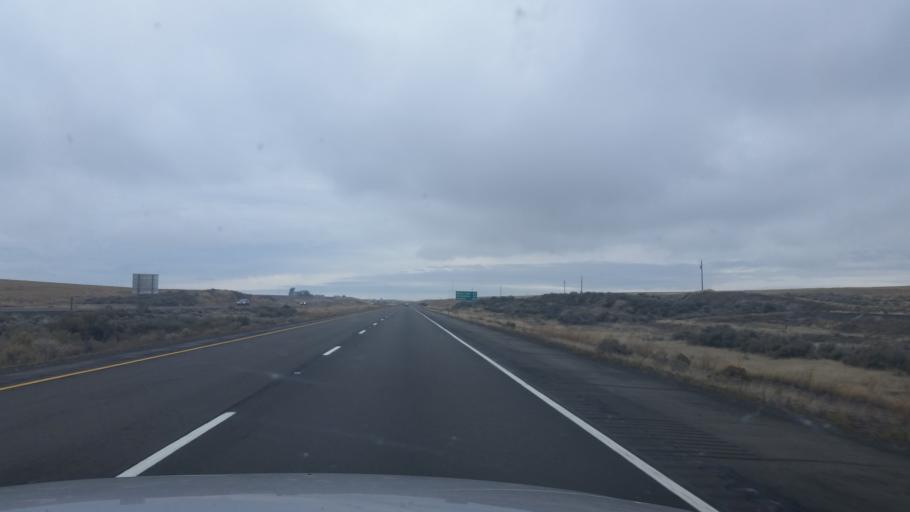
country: US
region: Washington
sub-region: Adams County
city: Ritzville
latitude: 47.1113
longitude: -118.4123
